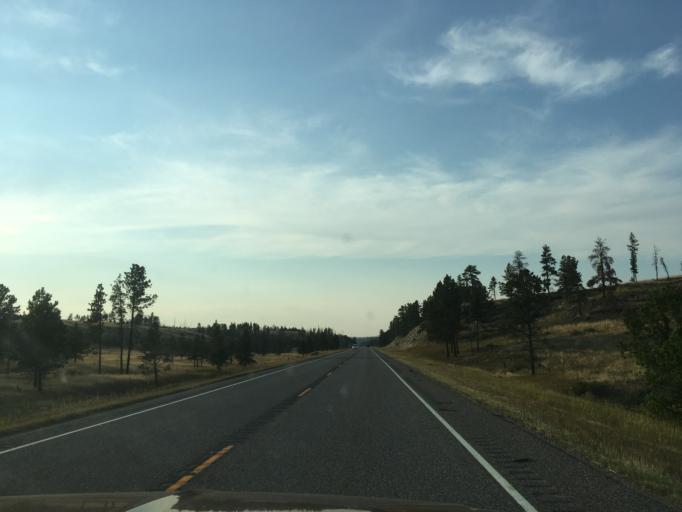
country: US
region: Montana
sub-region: Musselshell County
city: Roundup
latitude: 46.2702
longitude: -108.4710
